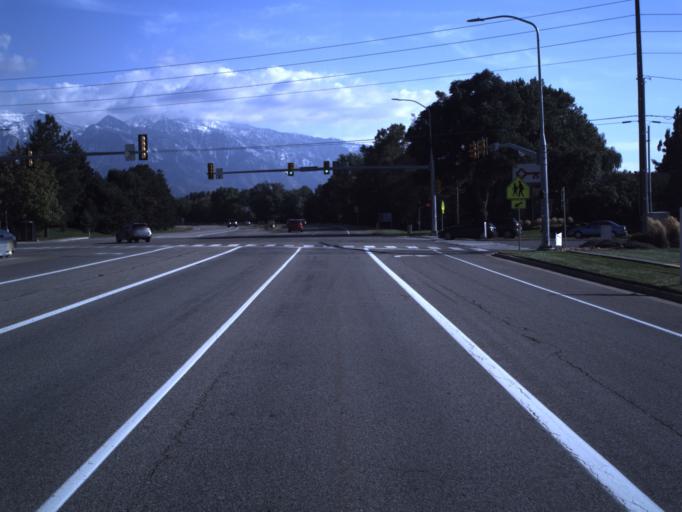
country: US
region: Utah
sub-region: Salt Lake County
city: Holladay
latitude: 40.6500
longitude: -111.8490
